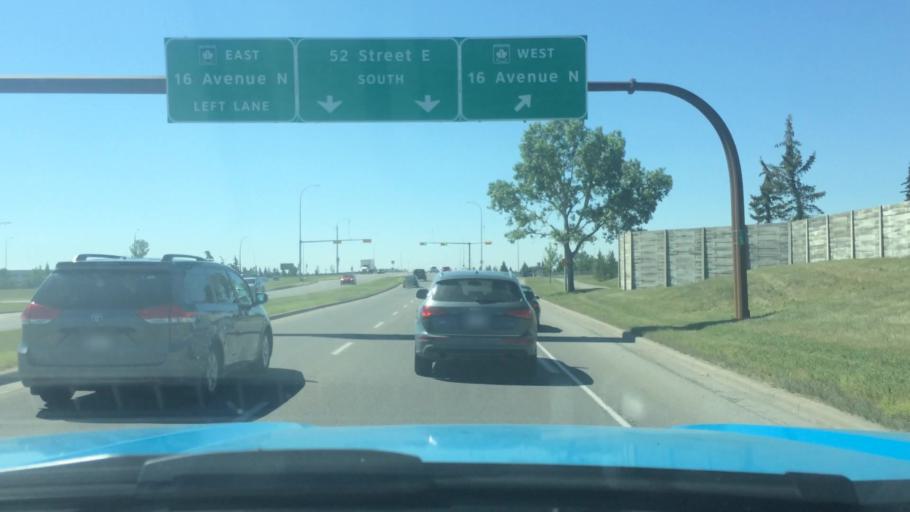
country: CA
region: Alberta
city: Calgary
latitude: 51.0695
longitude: -113.9585
